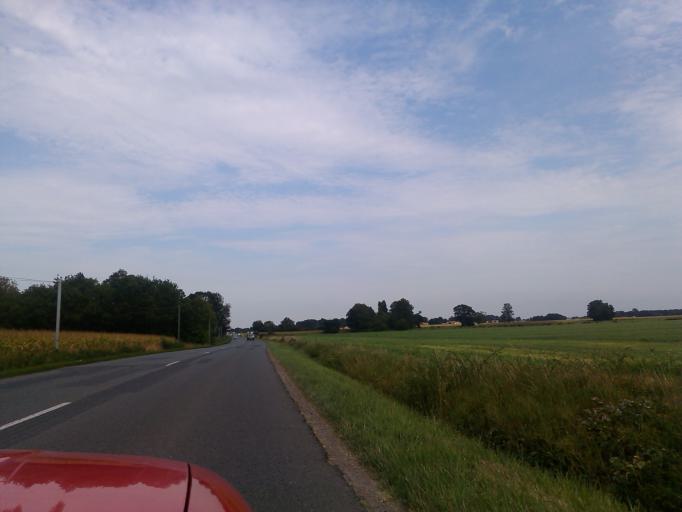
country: FR
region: Poitou-Charentes
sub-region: Departement de la Charente-Maritime
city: Medis
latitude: 45.6752
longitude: -0.9647
